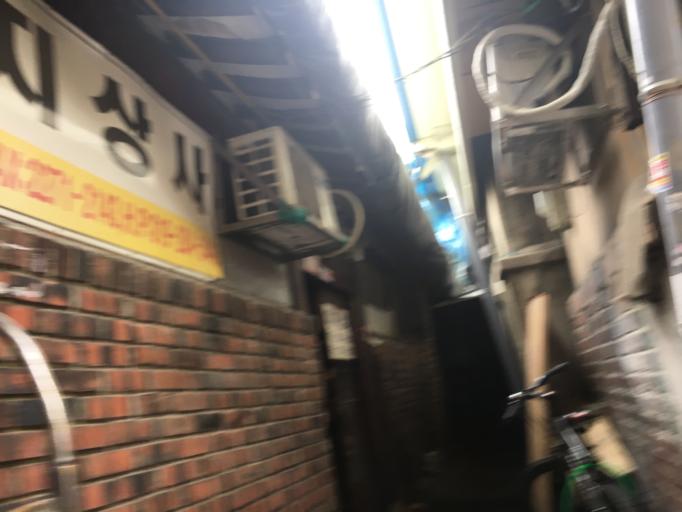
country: KR
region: Seoul
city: Seoul
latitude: 37.5678
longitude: 126.9912
